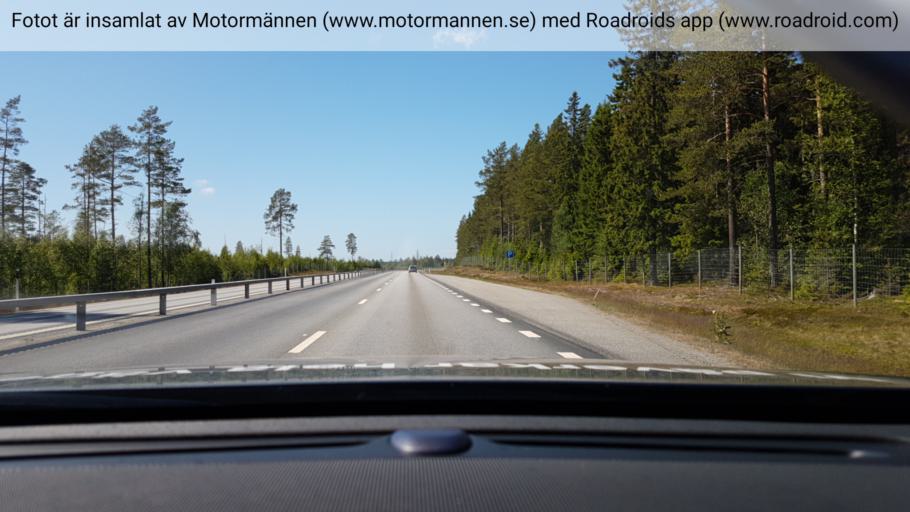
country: SE
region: Vaesterbotten
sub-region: Umea Kommun
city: Hoernefors
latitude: 63.6347
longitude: 19.8953
